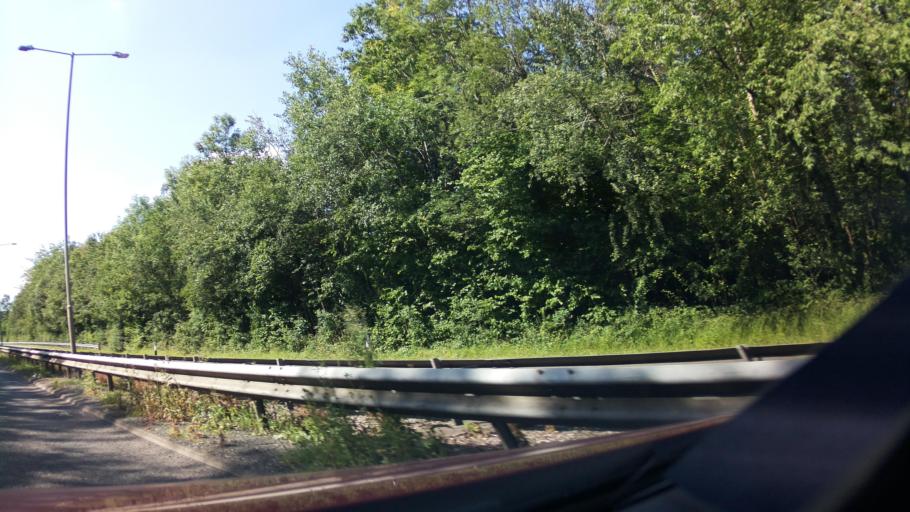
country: GB
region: England
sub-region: Worcestershire
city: Redditch
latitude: 52.3006
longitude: -1.9648
